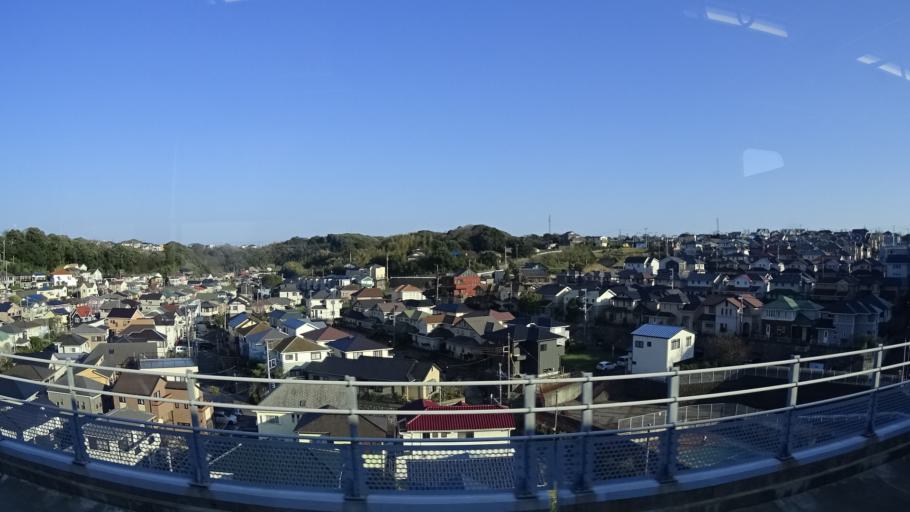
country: JP
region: Kanagawa
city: Miura
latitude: 35.1797
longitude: 139.6348
